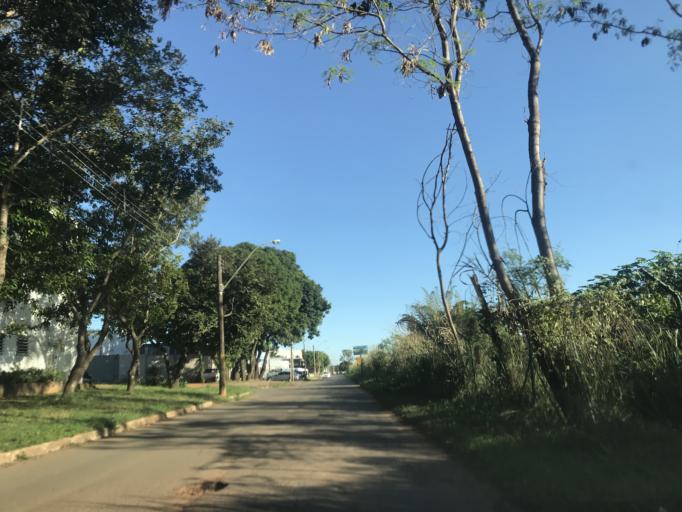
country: BR
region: Federal District
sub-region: Brasilia
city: Brasilia
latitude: -15.8221
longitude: -47.9580
